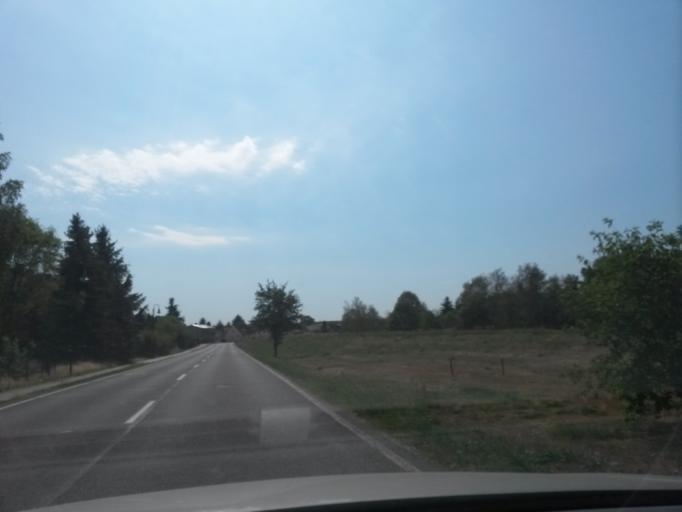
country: DE
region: Saxony-Anhalt
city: Jerichow
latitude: 52.4452
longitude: 12.0068
